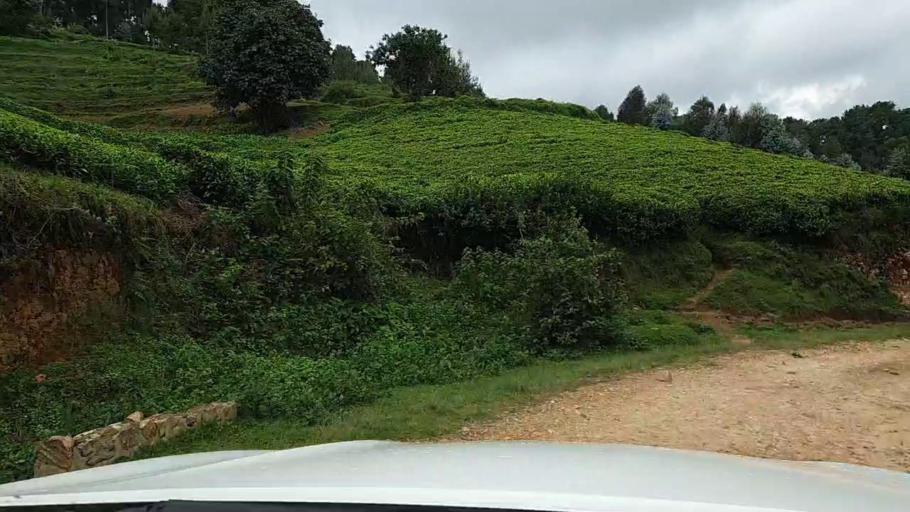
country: RW
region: Western Province
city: Kibuye
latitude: -2.2887
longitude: 29.3735
